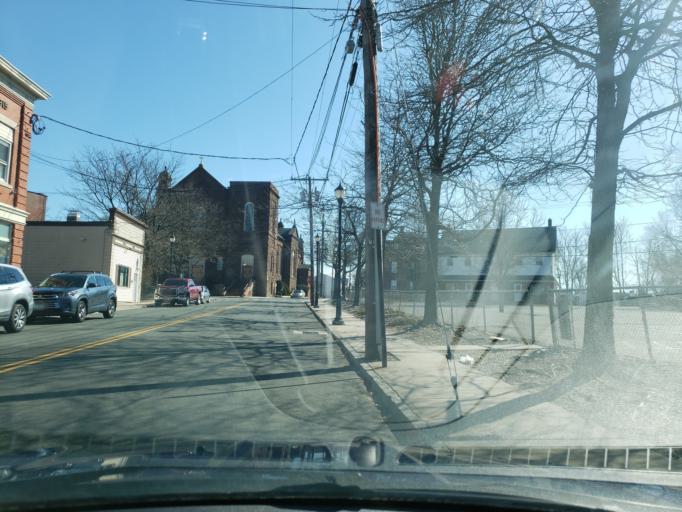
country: US
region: Connecticut
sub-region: Hartford County
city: Thompsonville
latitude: 41.9976
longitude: -72.5998
